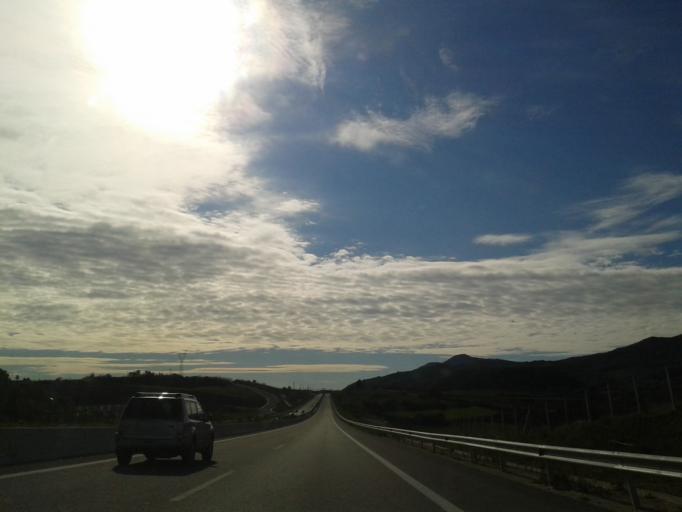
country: GR
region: West Greece
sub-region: Nomos Aitolias kai Akarnanias
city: Fitiai
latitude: 38.7123
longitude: 21.2085
